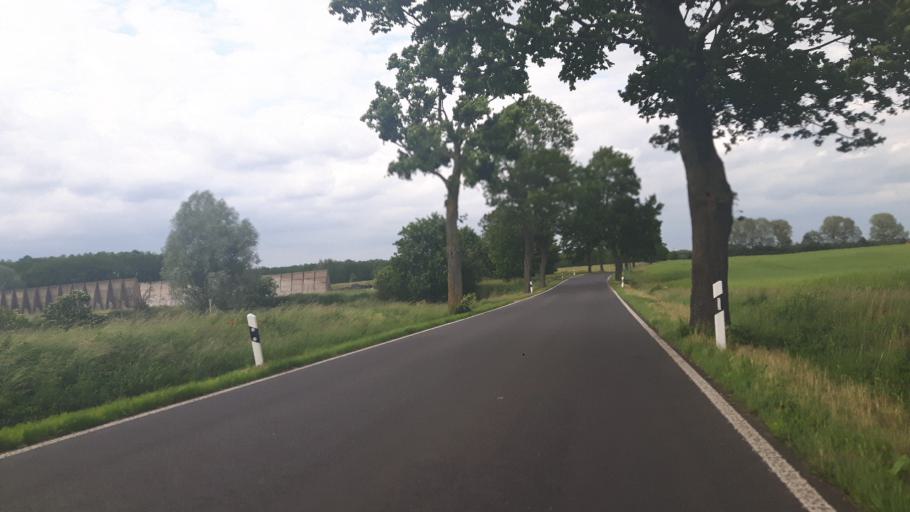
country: DE
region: Brandenburg
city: Eberswalde
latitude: 52.7639
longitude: 13.8144
